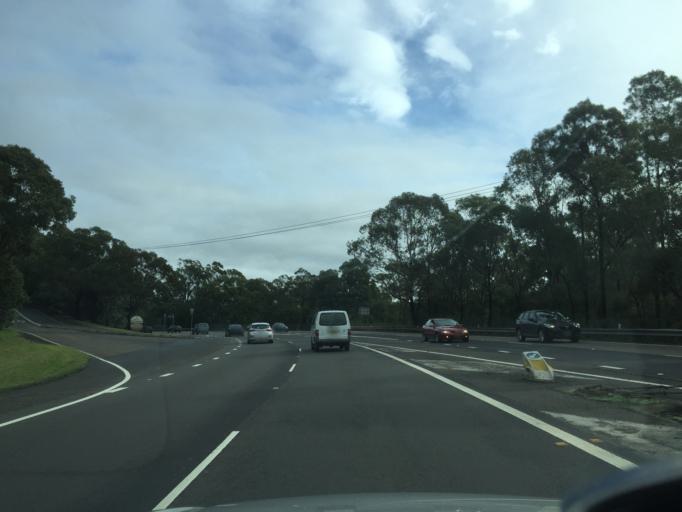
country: AU
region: New South Wales
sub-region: Blue Mountains Municipality
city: Glenbrook
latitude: -33.7639
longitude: 150.6341
